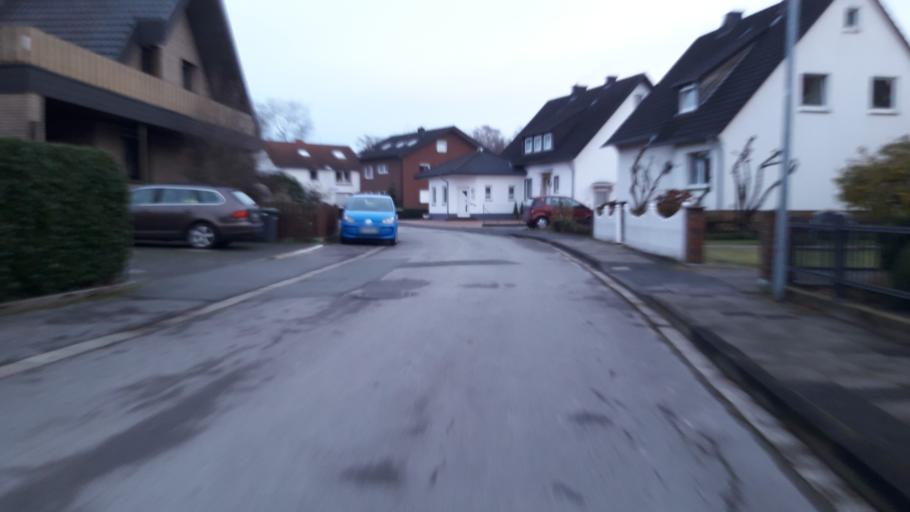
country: DE
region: North Rhine-Westphalia
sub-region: Regierungsbezirk Detmold
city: Hovelhof
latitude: 51.8212
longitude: 8.6495
